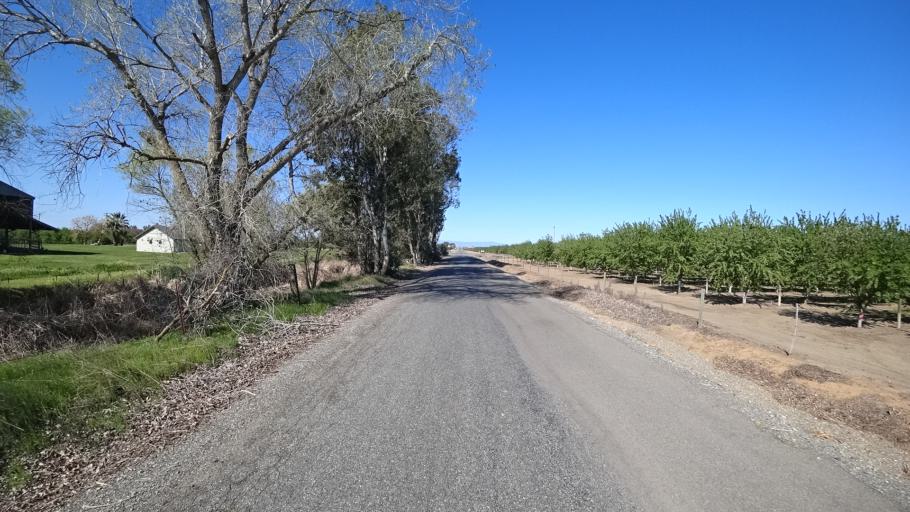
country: US
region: California
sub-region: Glenn County
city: Hamilton City
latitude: 39.7824
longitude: -122.0839
